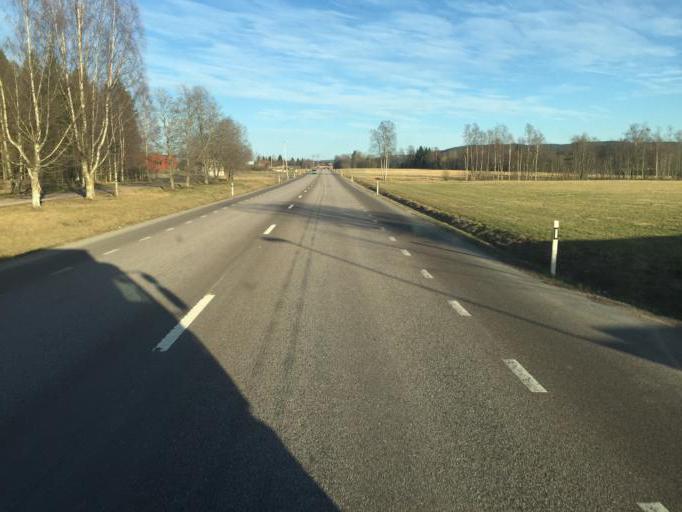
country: SE
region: Dalarna
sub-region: Gagnefs Kommun
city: Djuras
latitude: 60.5556
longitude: 15.1476
